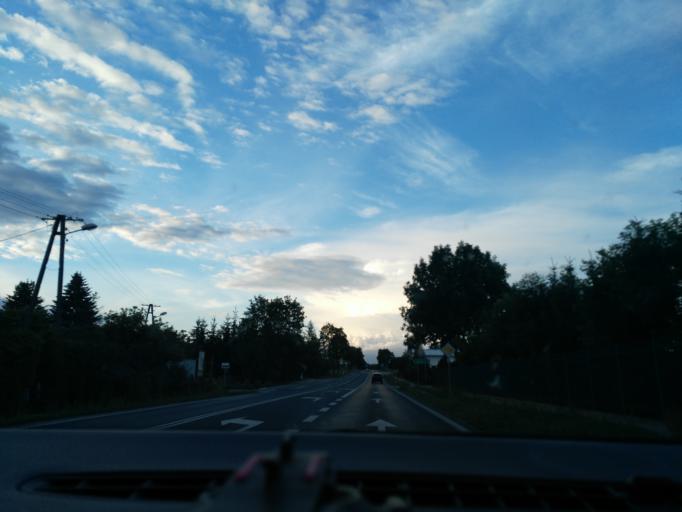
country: PL
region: Lublin Voivodeship
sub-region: Powiat lubelski
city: Niemce
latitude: 51.3643
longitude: 22.6306
